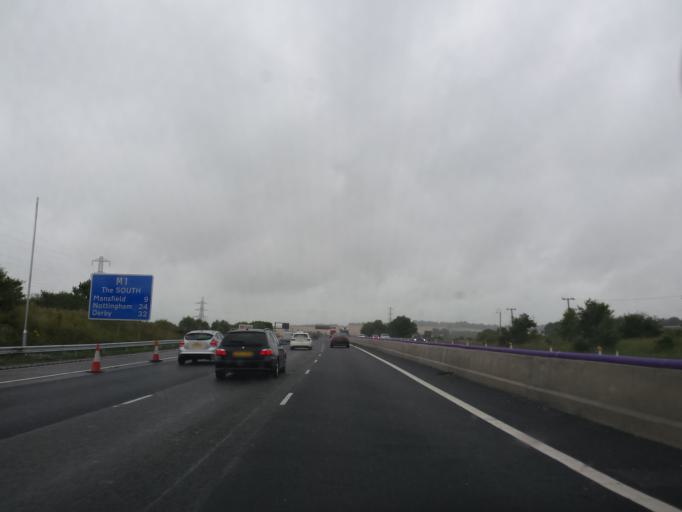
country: GB
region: England
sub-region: Derbyshire
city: Staveley
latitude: 53.2347
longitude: -1.3328
